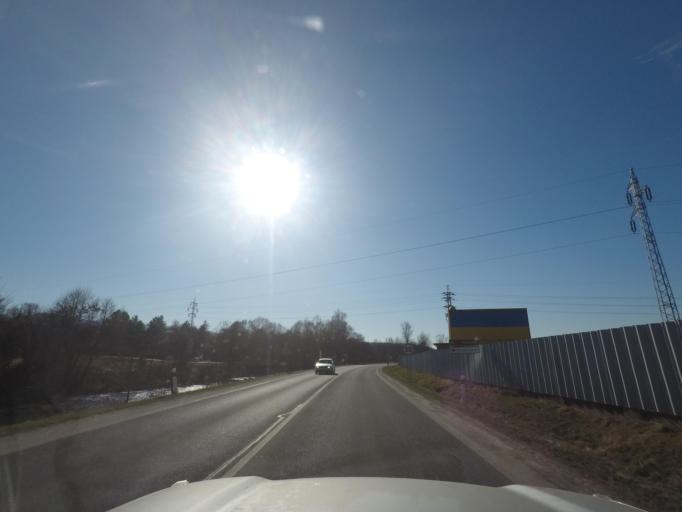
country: SK
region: Presovsky
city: Snina
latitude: 48.9828
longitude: 22.1802
